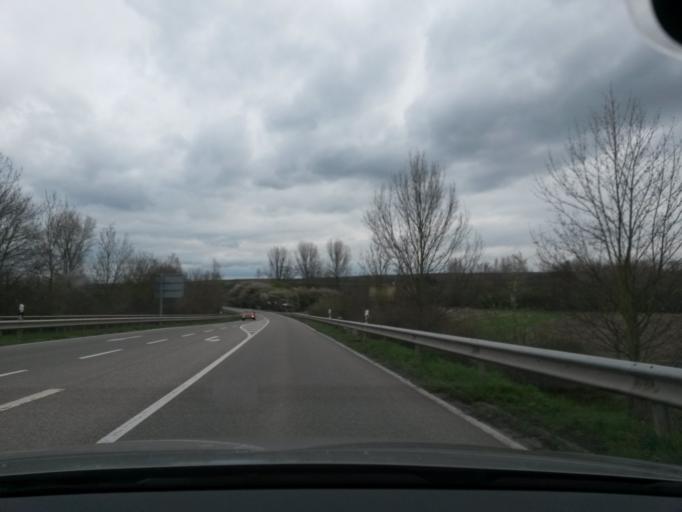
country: DE
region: Rheinland-Pfalz
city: Osthofen
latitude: 49.6723
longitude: 8.3003
